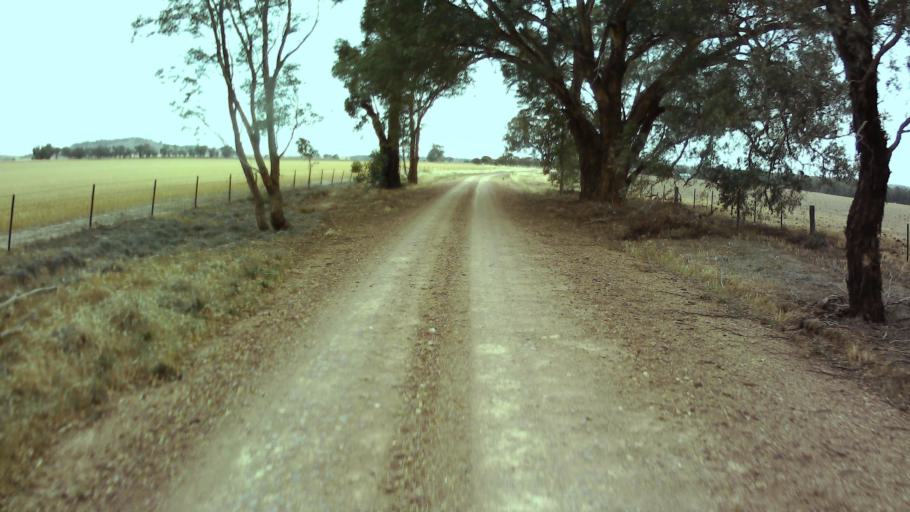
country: AU
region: New South Wales
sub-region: Weddin
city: Grenfell
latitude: -33.9175
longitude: 148.2876
